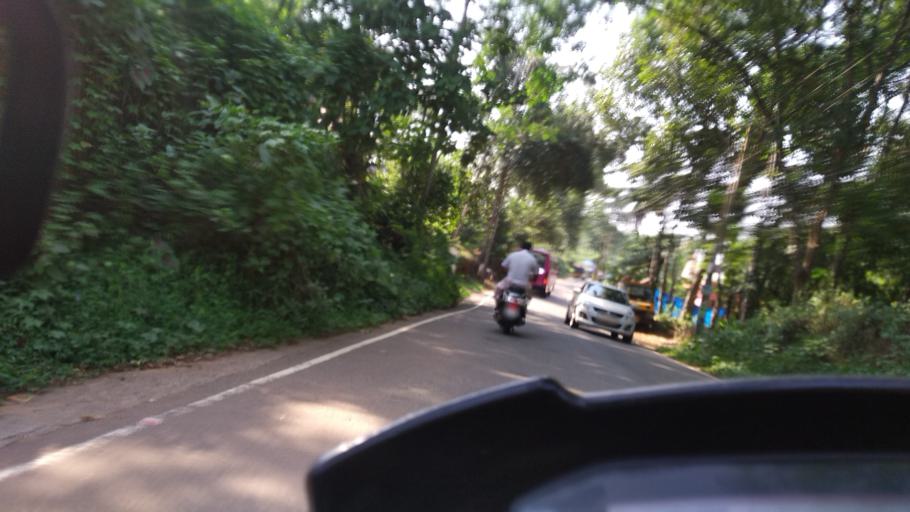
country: IN
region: Kerala
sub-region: Ernakulam
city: Piravam
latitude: 9.8126
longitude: 76.5615
